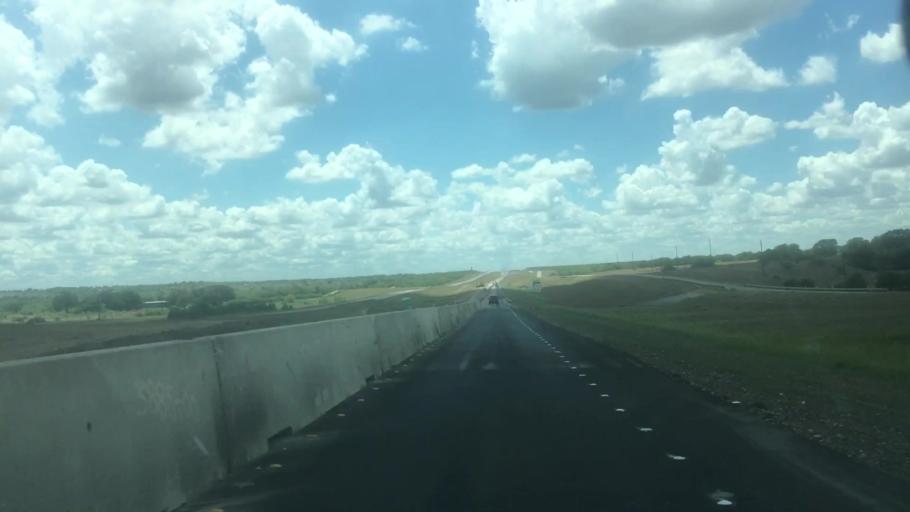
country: US
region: Texas
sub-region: Caldwell County
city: Lockhart
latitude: 29.8354
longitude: -97.7347
